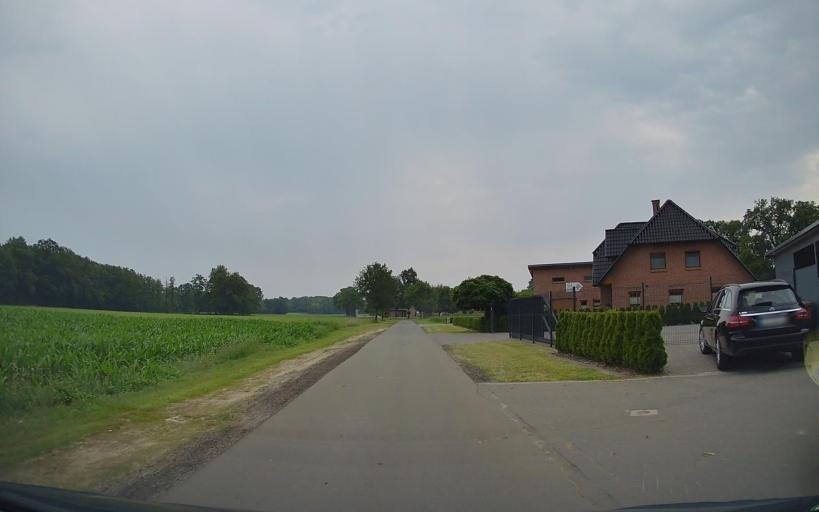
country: DE
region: Lower Saxony
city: Friesoythe
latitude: 53.0444
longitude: 7.8633
